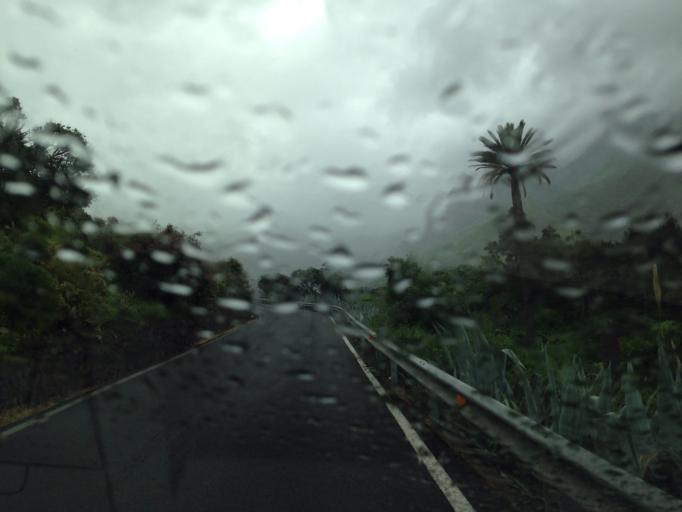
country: ES
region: Canary Islands
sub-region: Provincia de Las Palmas
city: Agaete
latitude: 28.0969
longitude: -15.6891
